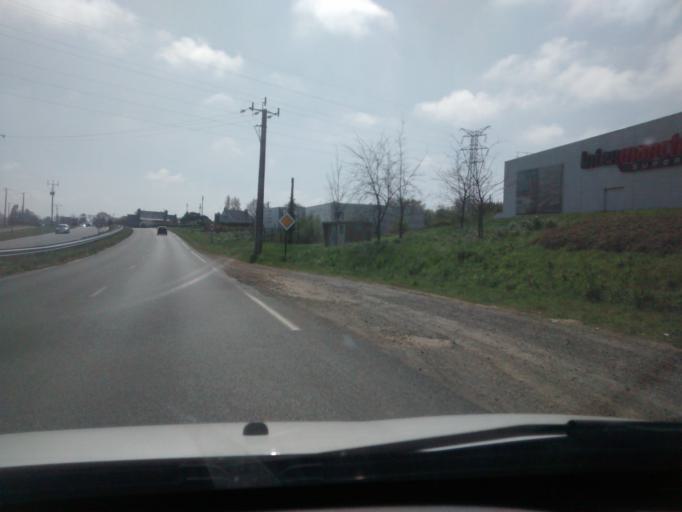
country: FR
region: Brittany
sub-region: Departement des Cotes-d'Armor
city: Saint-Quay-Perros
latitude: 48.7855
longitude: -3.4484
